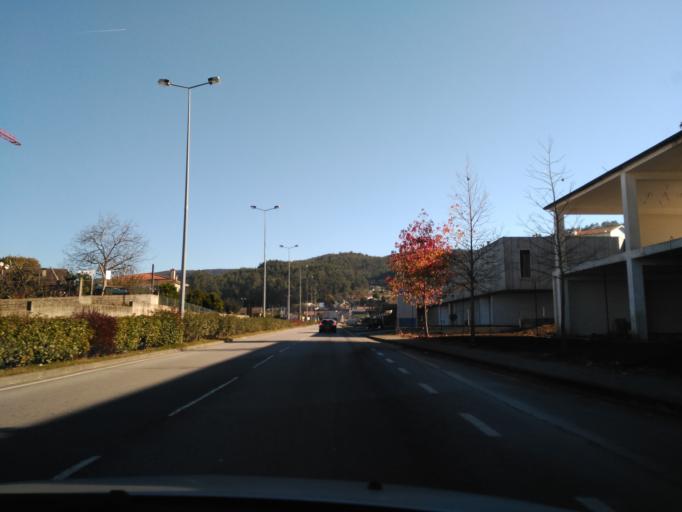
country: PT
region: Braga
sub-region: Braga
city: Adaufe
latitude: 41.5665
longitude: -8.3750
